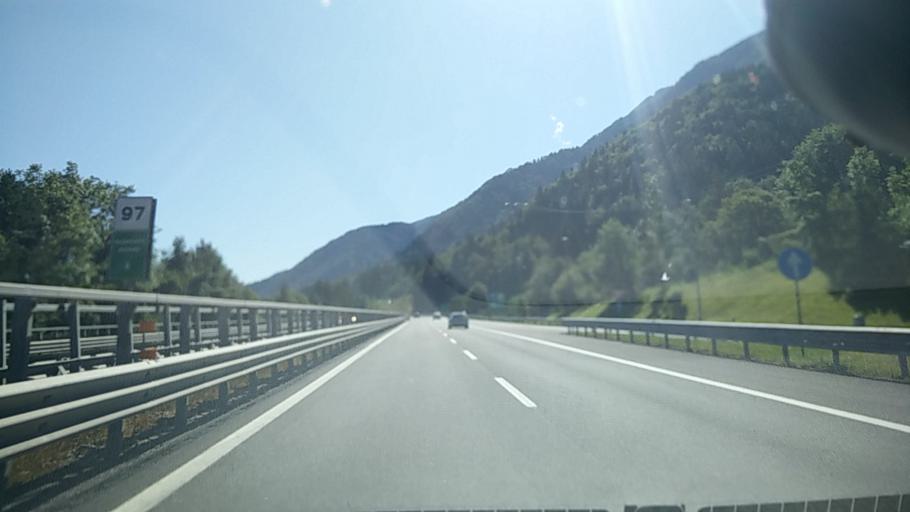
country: IT
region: Friuli Venezia Giulia
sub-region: Provincia di Udine
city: Malborghetto
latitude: 46.4989
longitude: 13.3776
